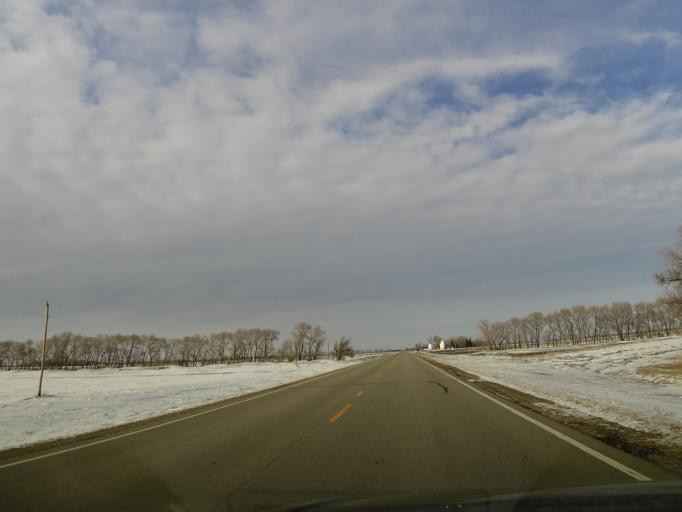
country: US
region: Minnesota
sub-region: Kittson County
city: Hallock
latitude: 48.5495
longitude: -97.1070
